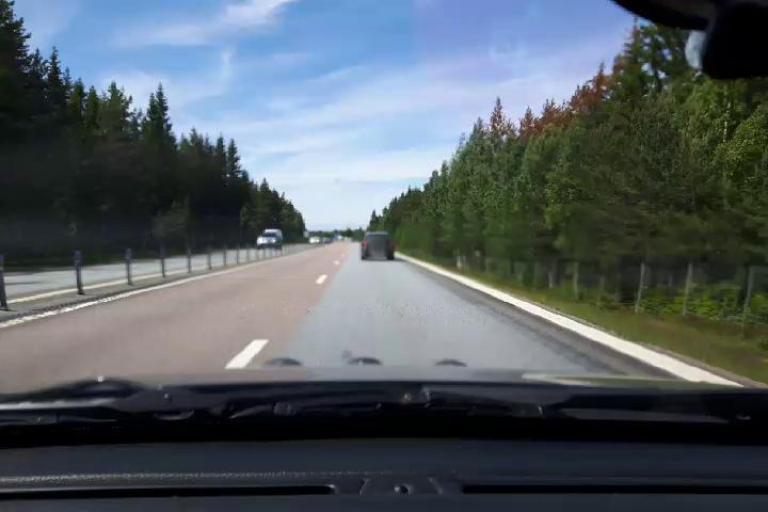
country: SE
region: Gaevleborg
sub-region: Gavle Kommun
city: Norrsundet
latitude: 60.8873
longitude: 17.0407
